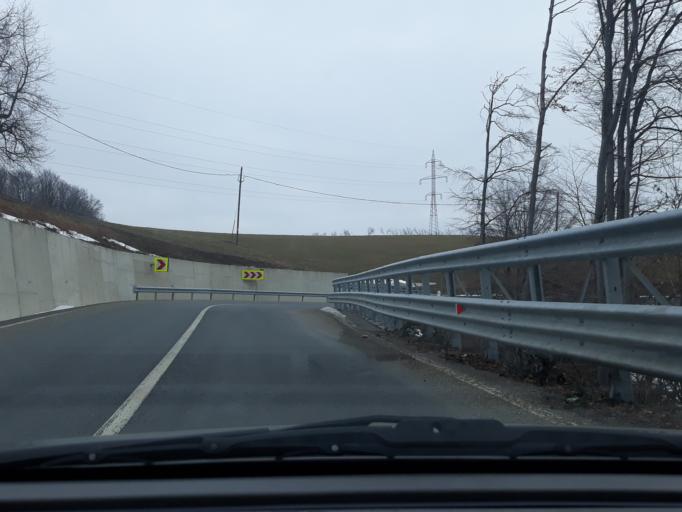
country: RO
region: Bihor
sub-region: Comuna Sinteu
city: Sinteu
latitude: 47.1227
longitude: 22.4638
